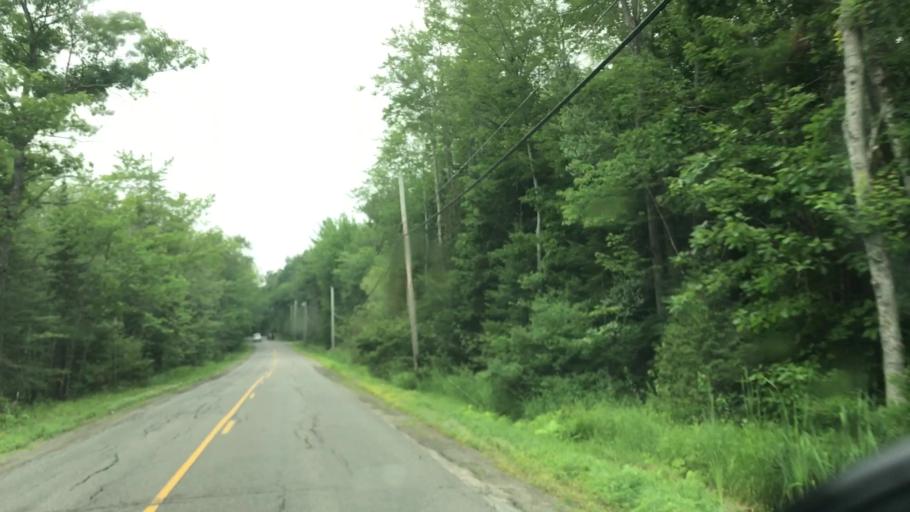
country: US
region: Maine
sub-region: Penobscot County
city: Orono
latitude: 44.8891
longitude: -68.7052
